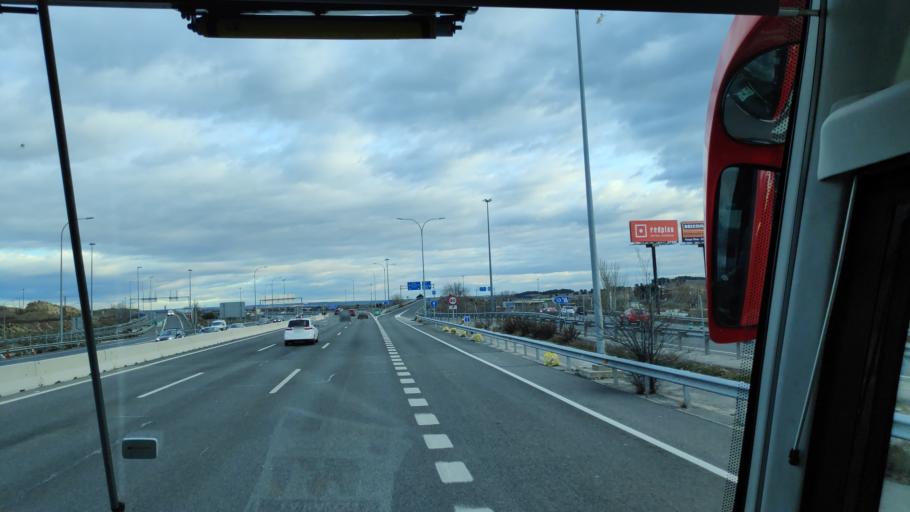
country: ES
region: Madrid
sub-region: Provincia de Madrid
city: Villa de Vallecas
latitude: 40.3628
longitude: -3.5721
